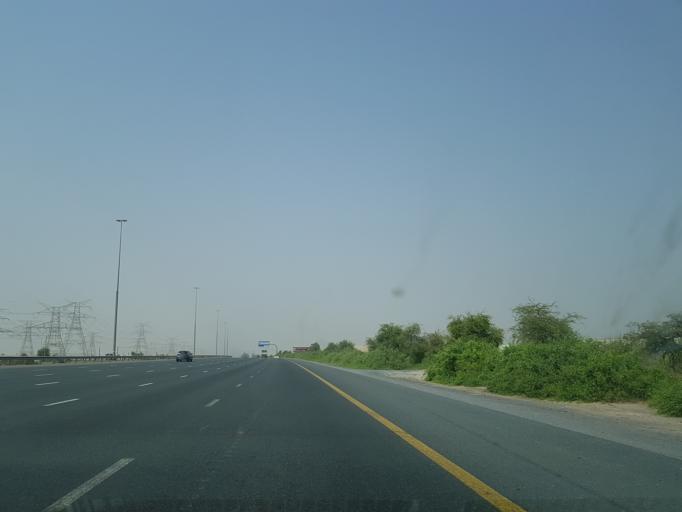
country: AE
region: Dubai
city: Dubai
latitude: 25.0550
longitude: 55.3147
